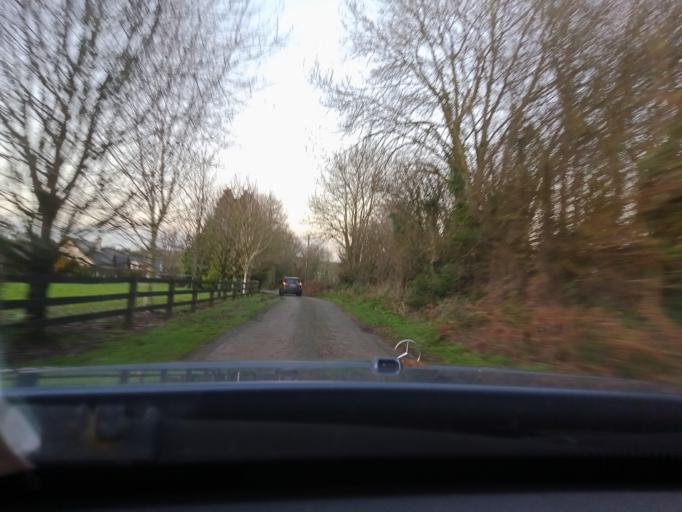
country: IE
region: Munster
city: Carrick-on-Suir
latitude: 52.4367
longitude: -7.3934
